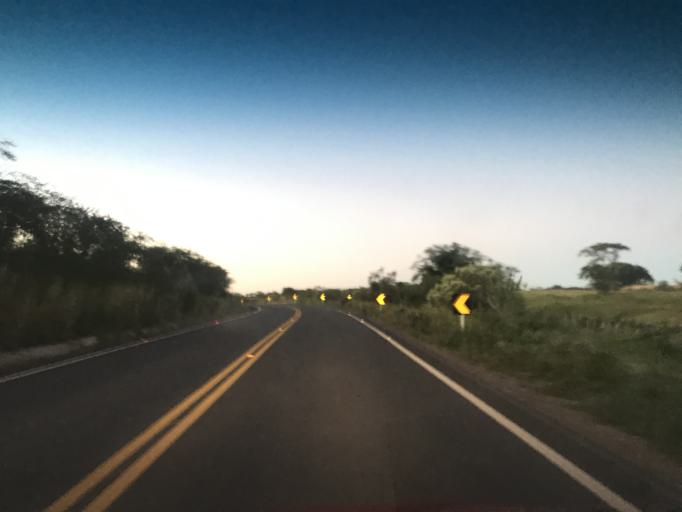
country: BR
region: Bahia
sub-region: Castro Alves
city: Castro Alves
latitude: -12.7511
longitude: -39.4062
